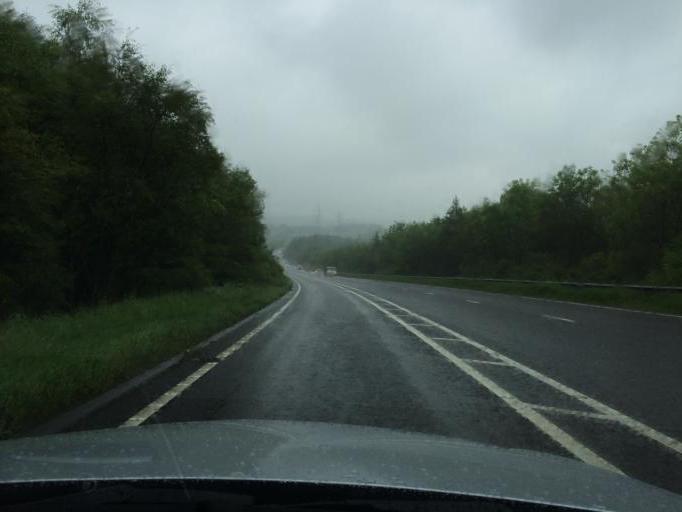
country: GB
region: England
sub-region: Barnsley
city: Wortley
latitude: 53.4852
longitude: -1.5544
